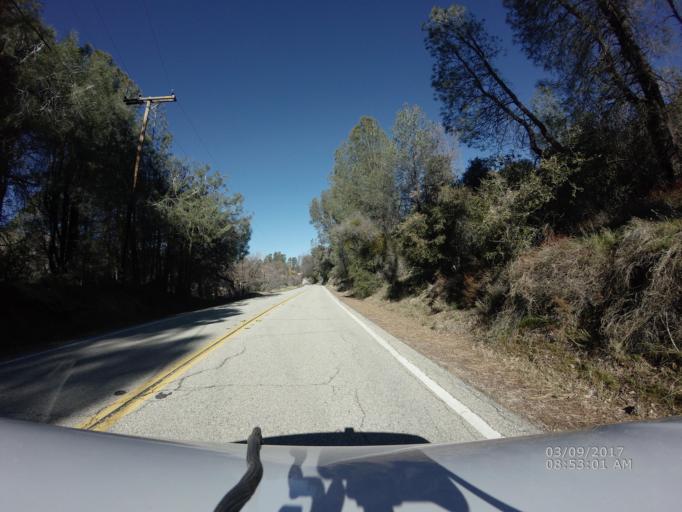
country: US
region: California
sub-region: Los Angeles County
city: Green Valley
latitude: 34.7111
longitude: -118.5547
